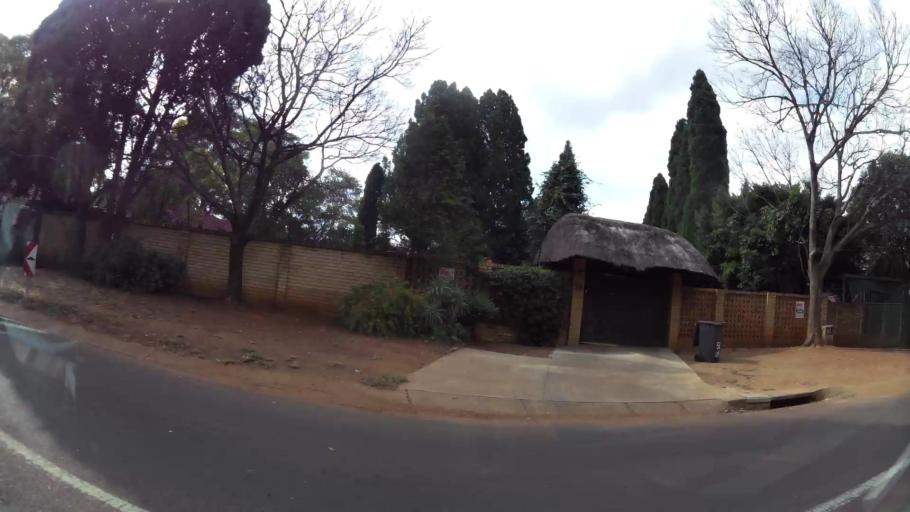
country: ZA
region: Gauteng
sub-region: City of Tshwane Metropolitan Municipality
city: Pretoria
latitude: -25.7569
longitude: 28.3145
